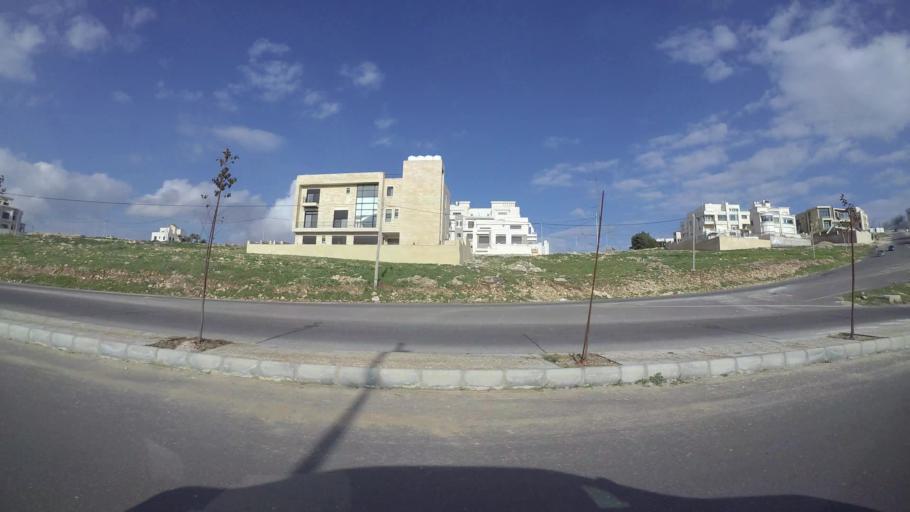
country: JO
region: Amman
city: Umm as Summaq
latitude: 31.9224
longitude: 35.8487
